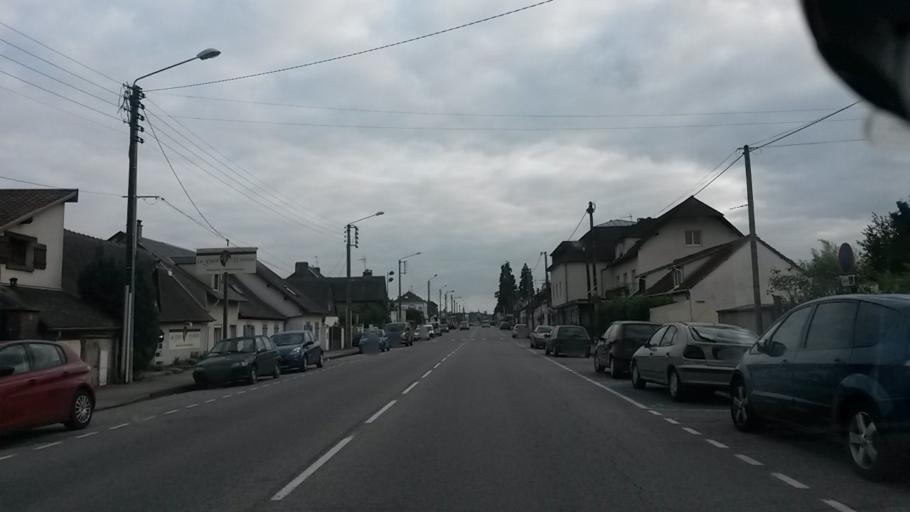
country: FR
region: Haute-Normandie
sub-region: Departement de l'Eure
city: Gravigny
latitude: 49.0434
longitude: 1.1602
